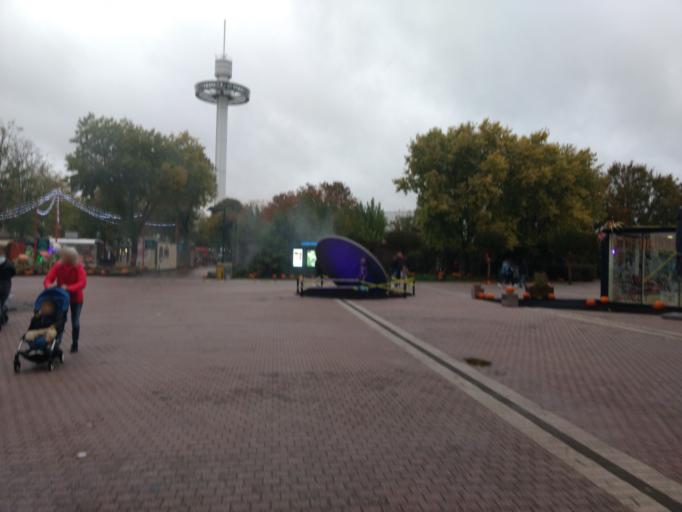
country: FR
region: Poitou-Charentes
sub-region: Departement de la Vienne
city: Jaunay-Clan
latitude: 46.6705
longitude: 0.3699
